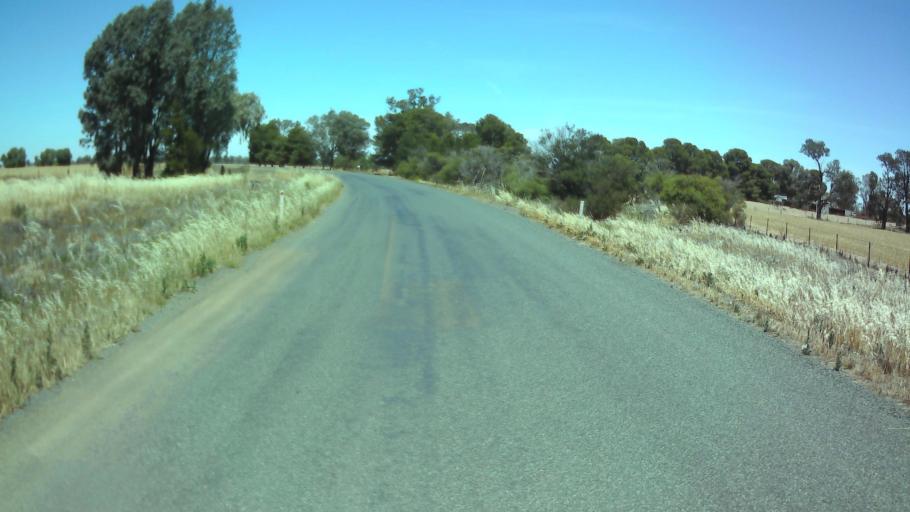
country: AU
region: New South Wales
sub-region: Weddin
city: Grenfell
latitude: -34.0456
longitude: 147.7834
